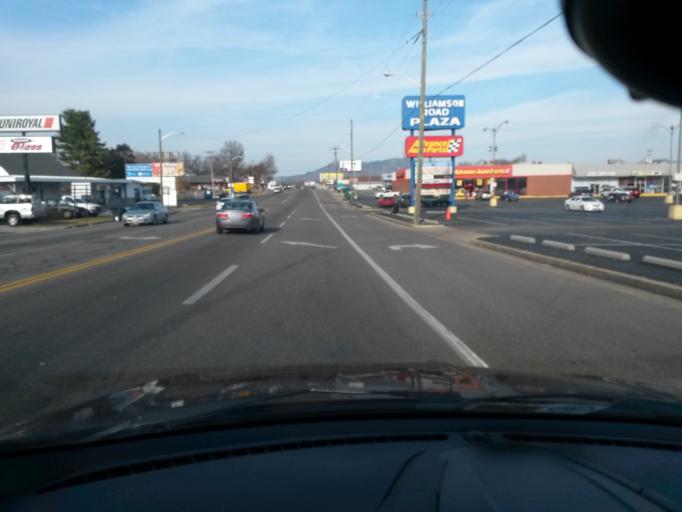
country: US
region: Virginia
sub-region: Roanoke County
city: Hollins
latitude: 37.3222
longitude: -79.9541
